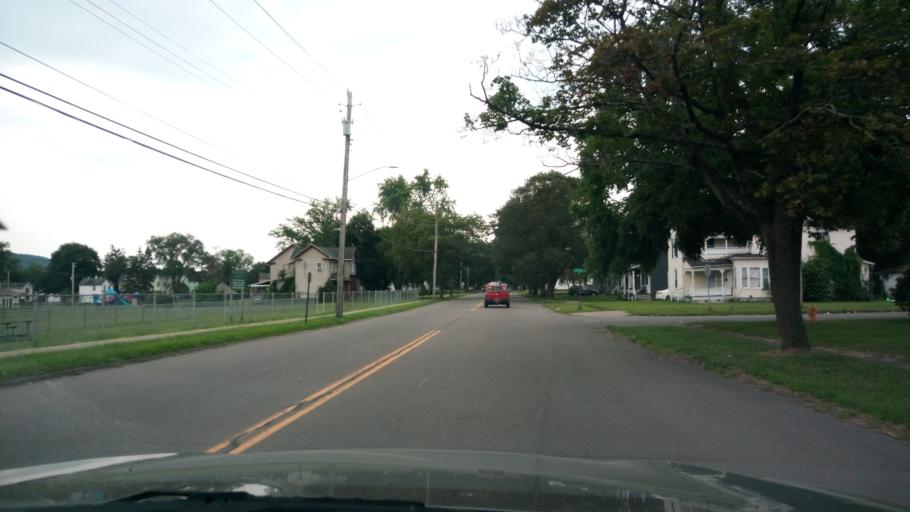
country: US
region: New York
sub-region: Chemung County
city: Elmira Heights
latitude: 42.1124
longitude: -76.8074
